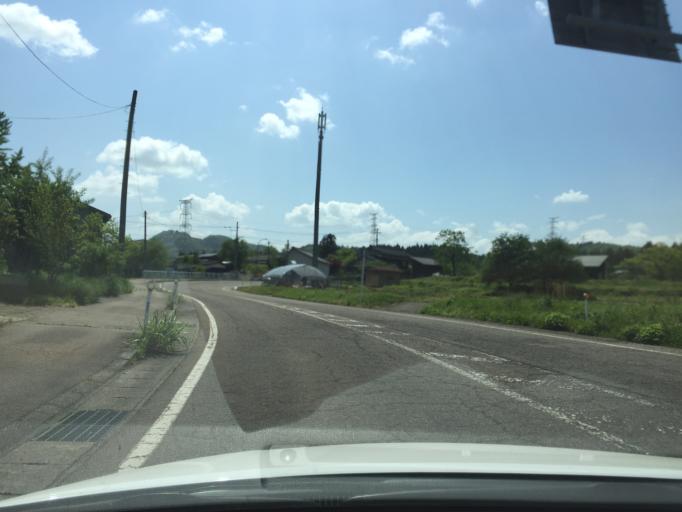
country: JP
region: Niigata
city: Tochio-honcho
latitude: 37.5443
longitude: 139.0919
